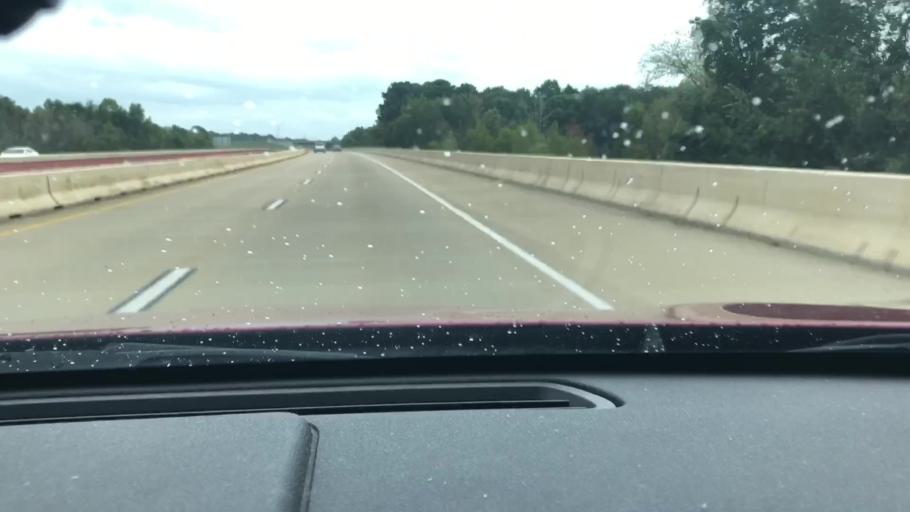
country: US
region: Texas
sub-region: Bowie County
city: Texarkana
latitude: 33.3855
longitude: -94.0545
